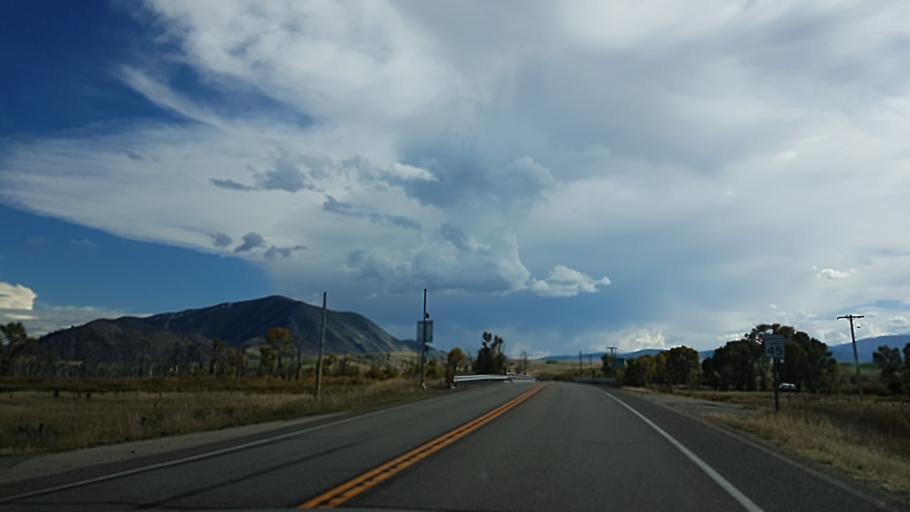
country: US
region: Montana
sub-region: Jefferson County
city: Whitehall
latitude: 45.8560
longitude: -111.9514
